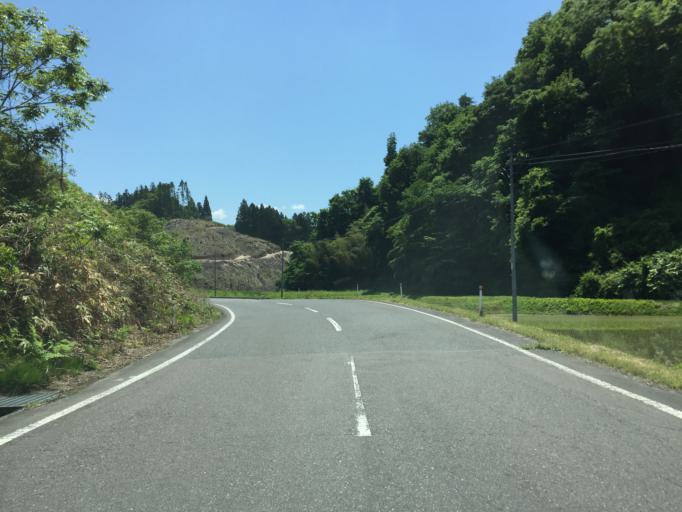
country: JP
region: Fukushima
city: Miharu
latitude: 37.4900
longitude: 140.5154
